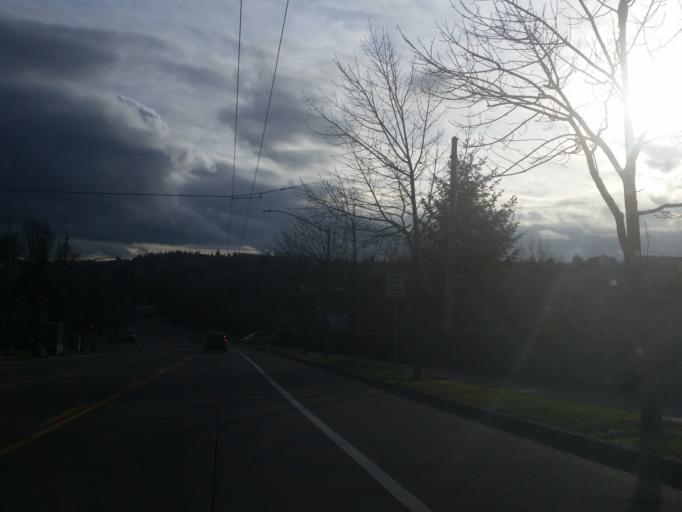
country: US
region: Washington
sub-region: King County
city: Seattle
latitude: 47.5893
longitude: -122.2978
